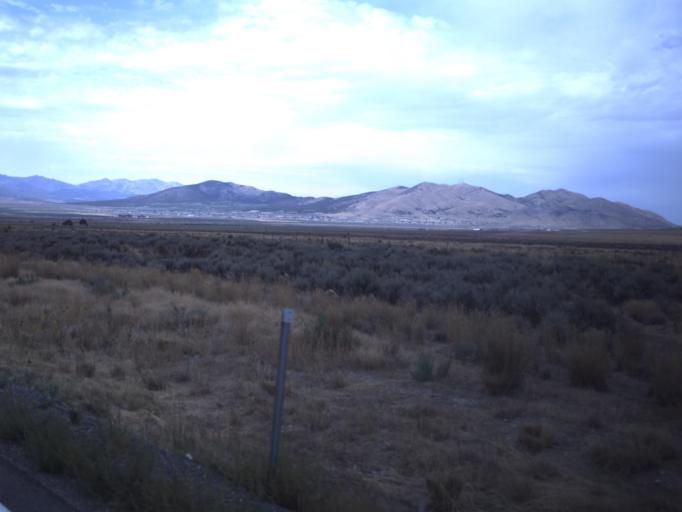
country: US
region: Utah
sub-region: Tooele County
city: Tooele
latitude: 40.3748
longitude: -112.3690
